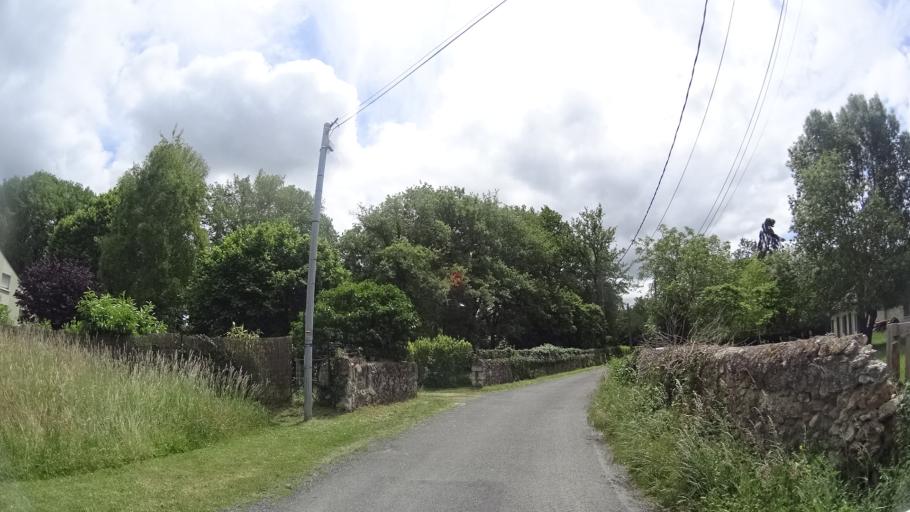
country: FR
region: Pays de la Loire
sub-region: Departement de Maine-et-Loire
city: Chenehutte-Treves-Cunault
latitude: 47.3030
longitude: -0.1531
